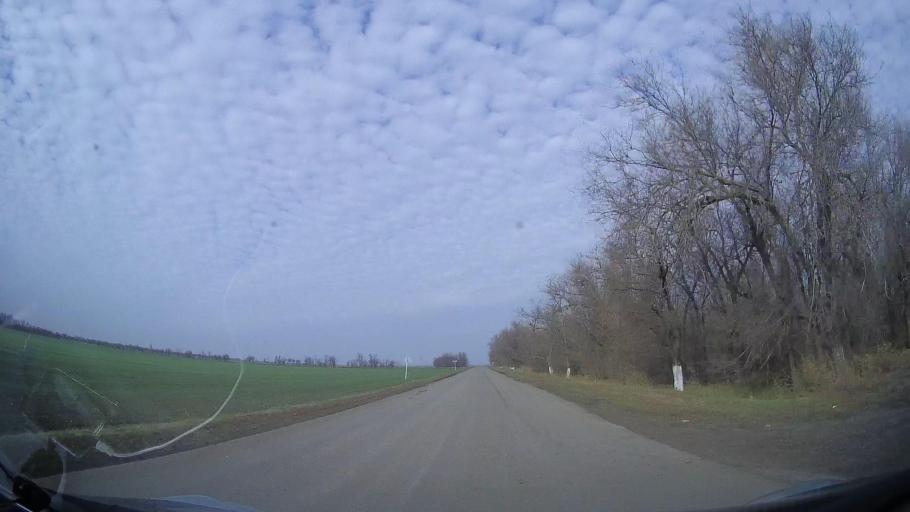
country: RU
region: Rostov
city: Gigant
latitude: 46.9254
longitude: 41.2469
